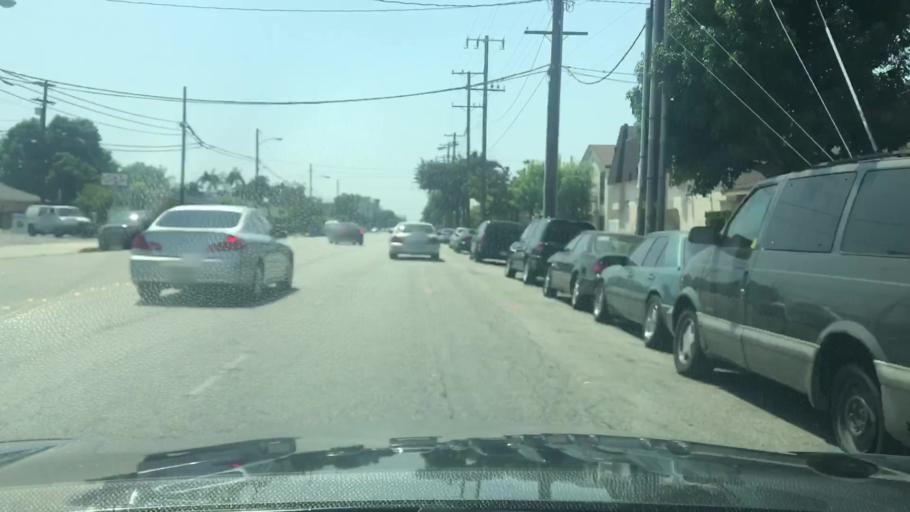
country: US
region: California
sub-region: Los Angeles County
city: Bellflower
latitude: 33.8880
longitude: -118.1174
